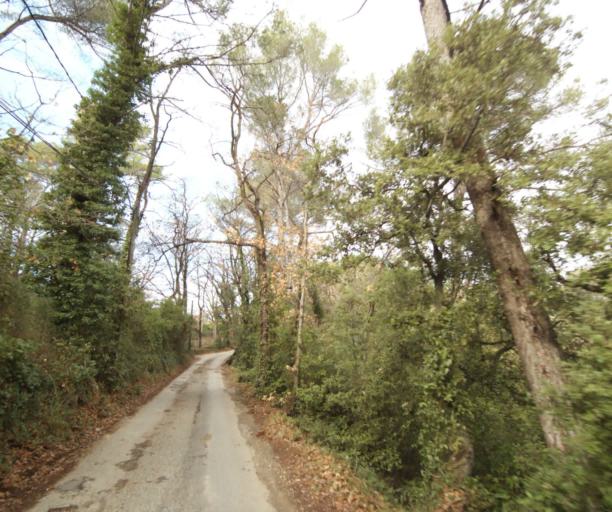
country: FR
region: Provence-Alpes-Cote d'Azur
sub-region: Departement du Var
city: Trans-en-Provence
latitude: 43.5137
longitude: 6.4952
